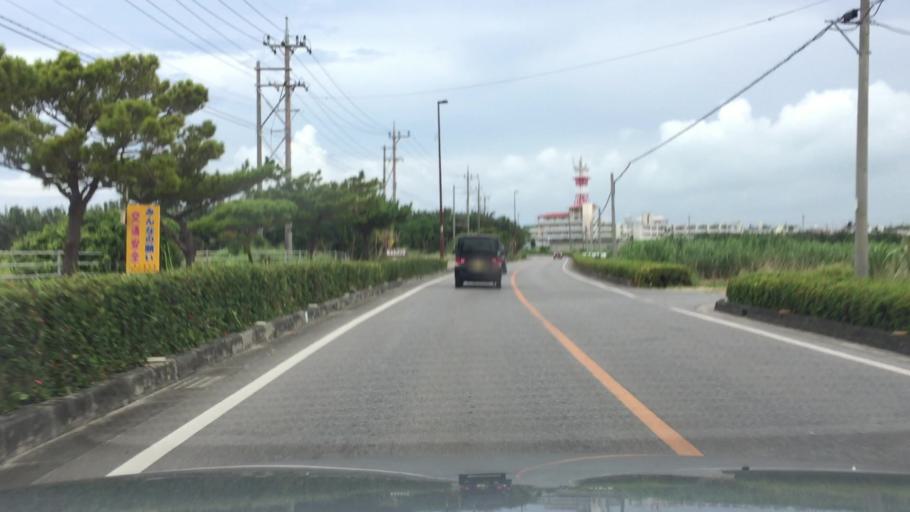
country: JP
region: Okinawa
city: Ishigaki
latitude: 24.3549
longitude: 124.1576
